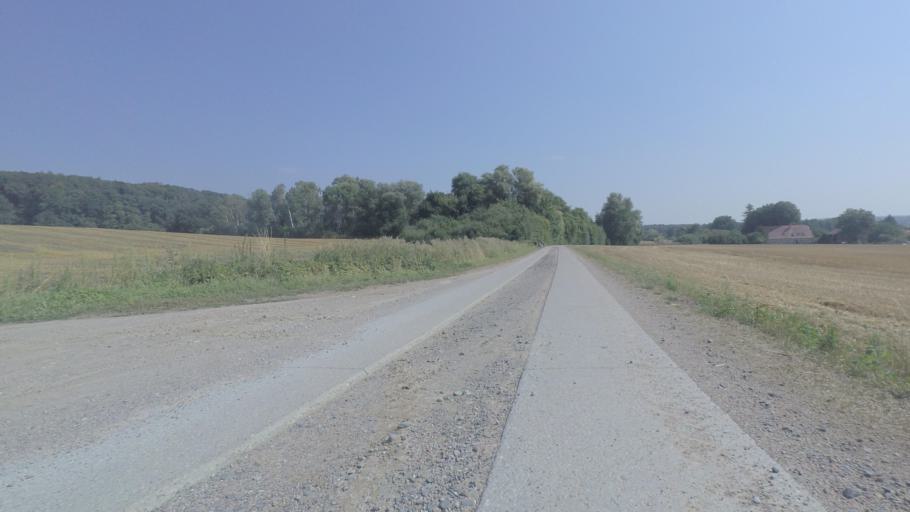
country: DE
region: Mecklenburg-Vorpommern
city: Pampow
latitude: 53.7235
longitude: 12.6483
